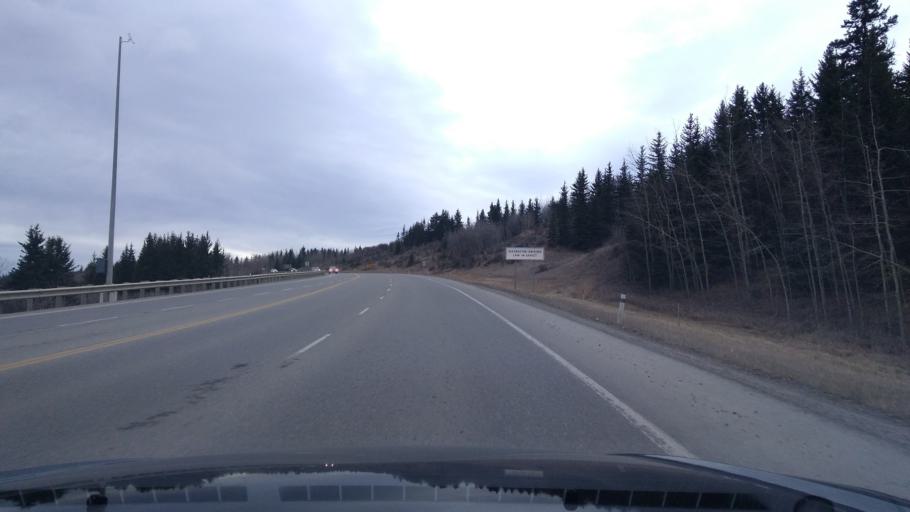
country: CA
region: Alberta
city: Cochrane
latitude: 51.1793
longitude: -114.4877
